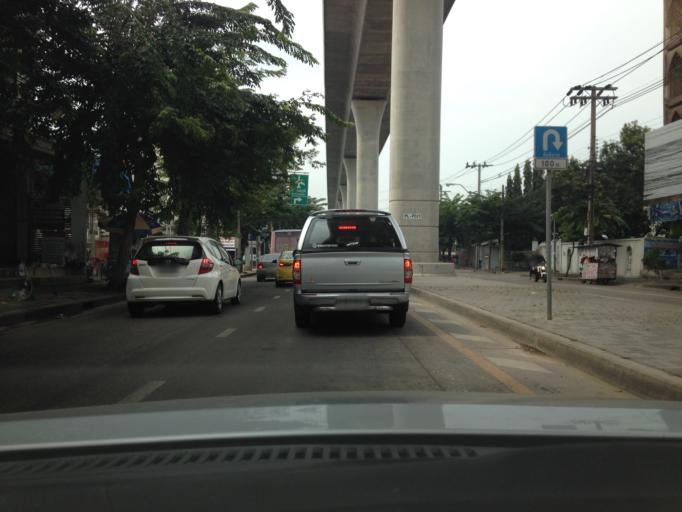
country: TH
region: Bangkok
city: Bang Sue
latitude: 13.8260
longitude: 100.5311
